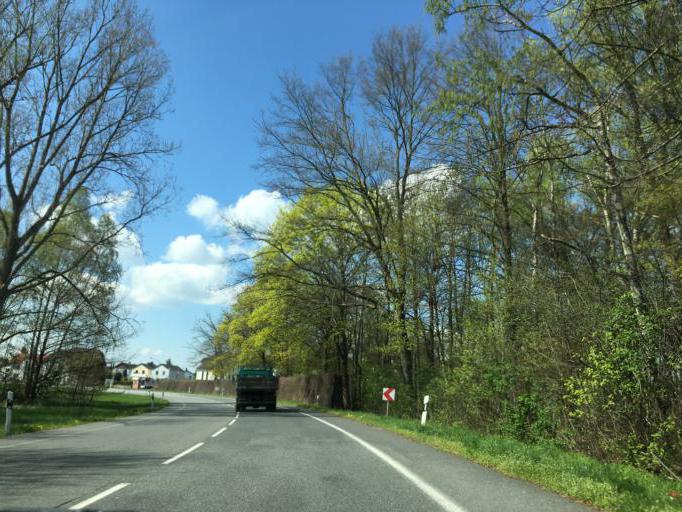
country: DE
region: Hesse
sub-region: Regierungsbezirk Darmstadt
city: Eppertshausen
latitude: 49.9855
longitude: 8.8283
